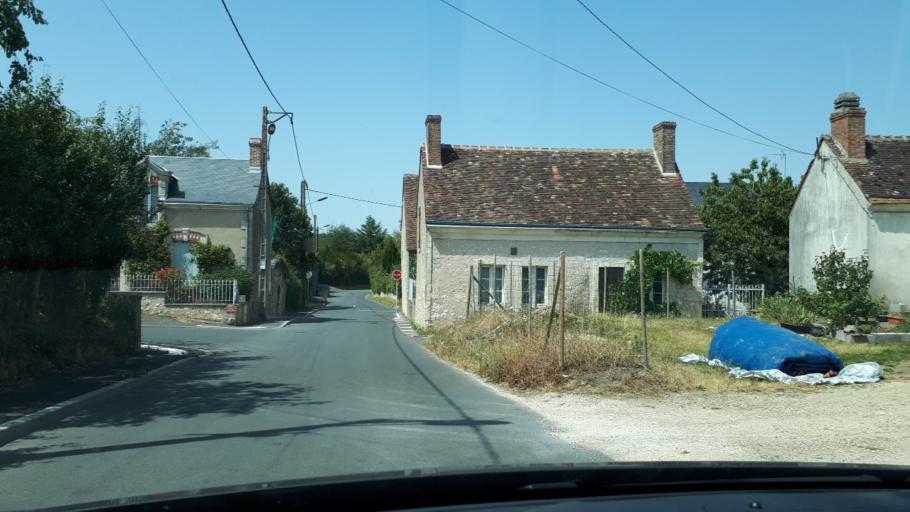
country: FR
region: Centre
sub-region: Departement du Loir-et-Cher
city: Vendome
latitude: 47.8167
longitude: 1.0595
